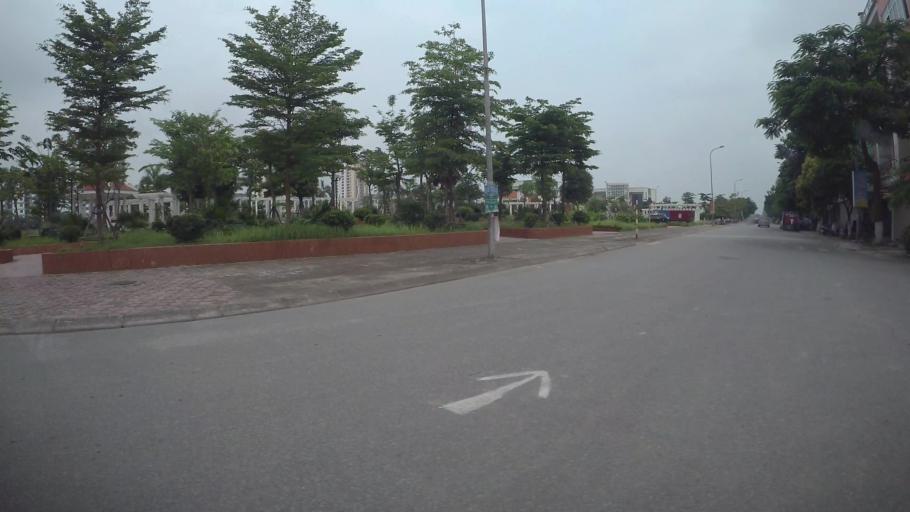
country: VN
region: Ha Noi
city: Trau Quy
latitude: 21.0633
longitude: 105.9159
